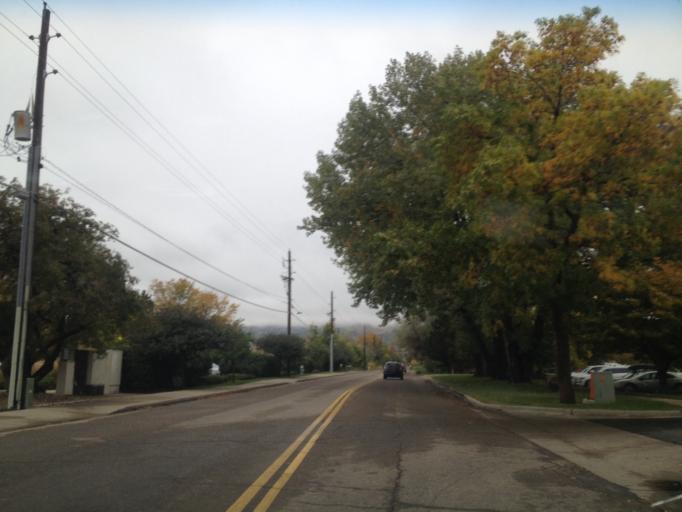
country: US
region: Colorado
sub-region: Boulder County
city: Boulder
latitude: 40.0365
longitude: -105.2542
